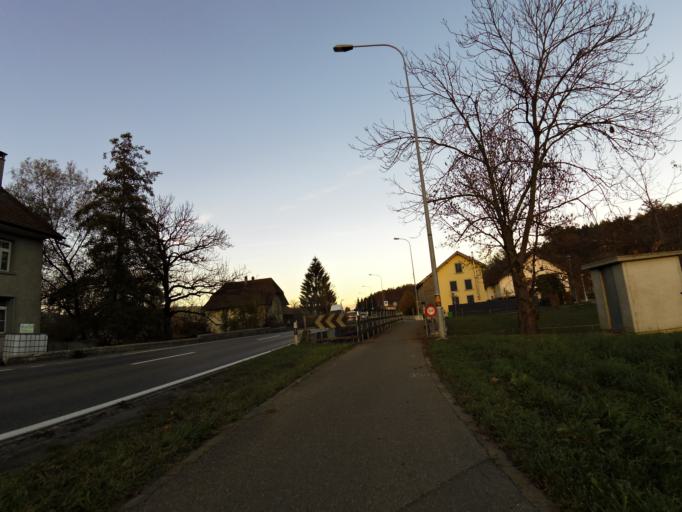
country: CH
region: Aargau
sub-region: Bezirk Aarau
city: Suhr
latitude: 47.3767
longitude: 8.0873
